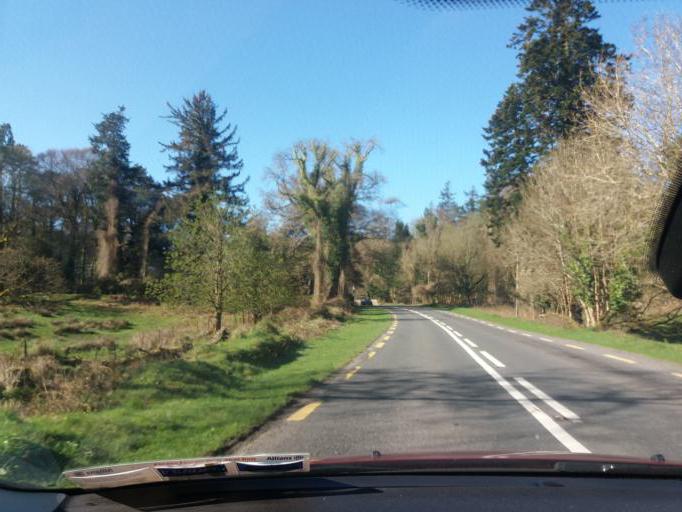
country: IE
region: Munster
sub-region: Ciarrai
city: Cill Airne
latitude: 52.0226
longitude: -9.4923
